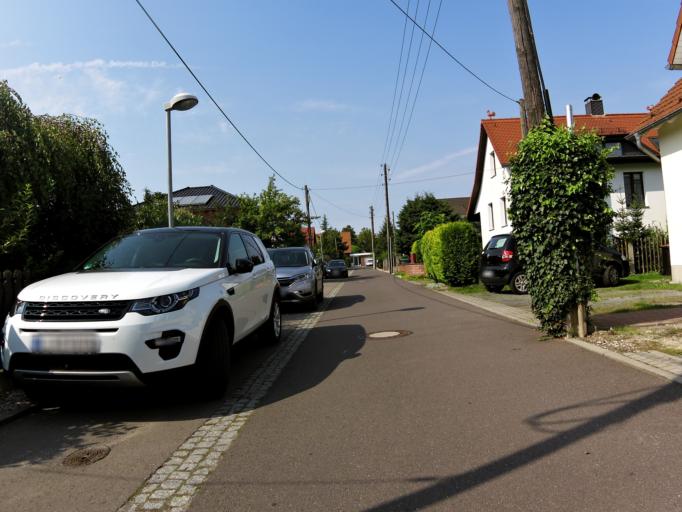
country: DE
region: Saxony
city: Rackwitz
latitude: 51.3908
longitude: 12.3833
